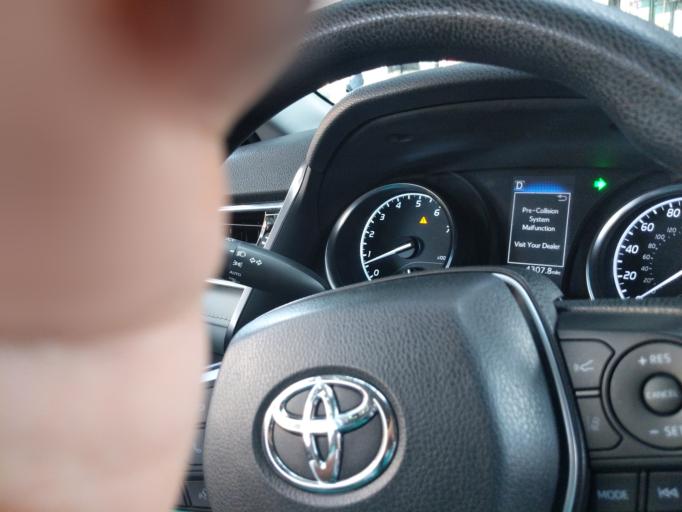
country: US
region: New York
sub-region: Bronx
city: The Bronx
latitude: 40.8655
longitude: -73.8674
